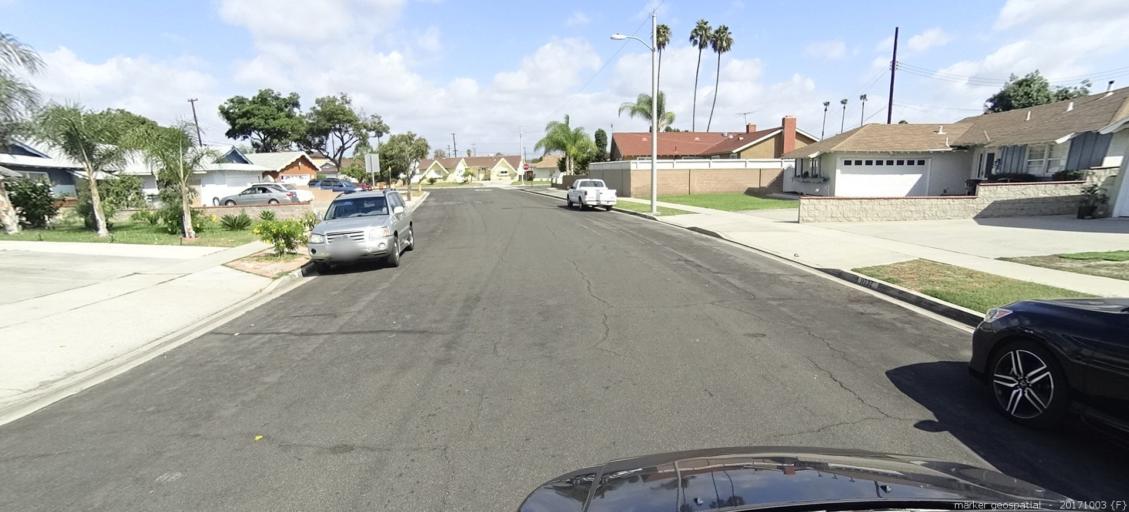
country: US
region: California
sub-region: Orange County
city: Garden Grove
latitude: 33.7684
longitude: -117.9251
